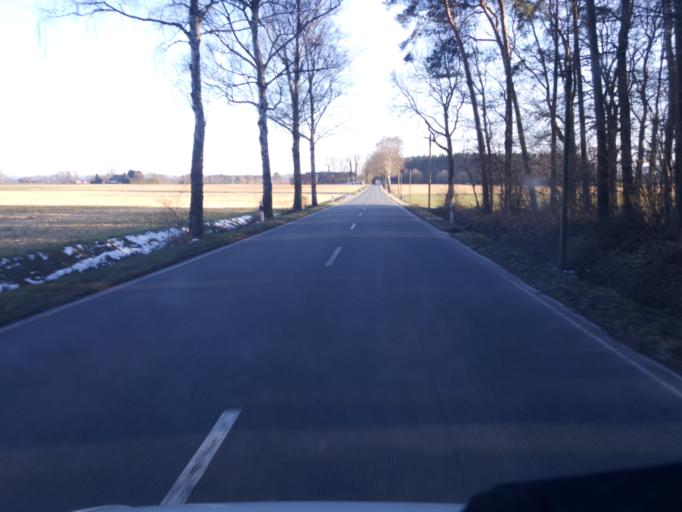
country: DE
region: North Rhine-Westphalia
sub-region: Regierungsbezirk Detmold
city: Hille
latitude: 52.3808
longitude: 8.7258
